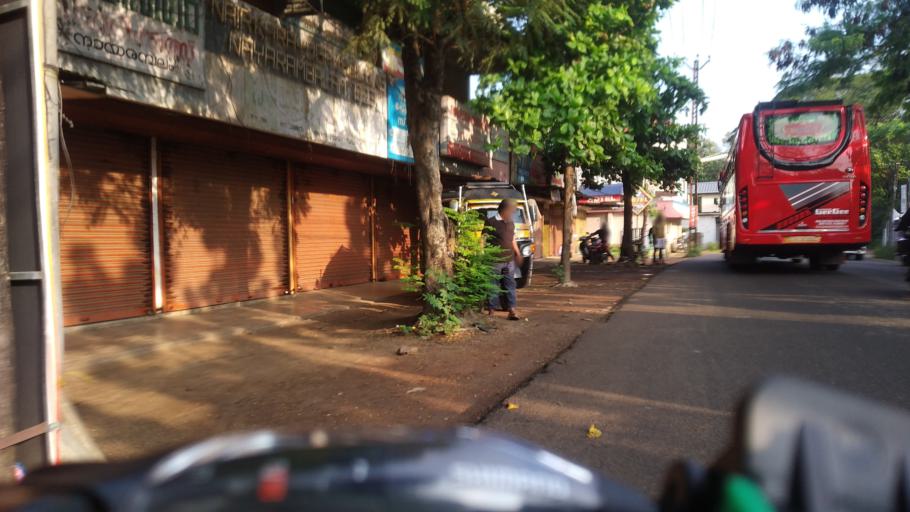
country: IN
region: Kerala
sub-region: Ernakulam
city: Elur
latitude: 10.0719
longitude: 76.2118
